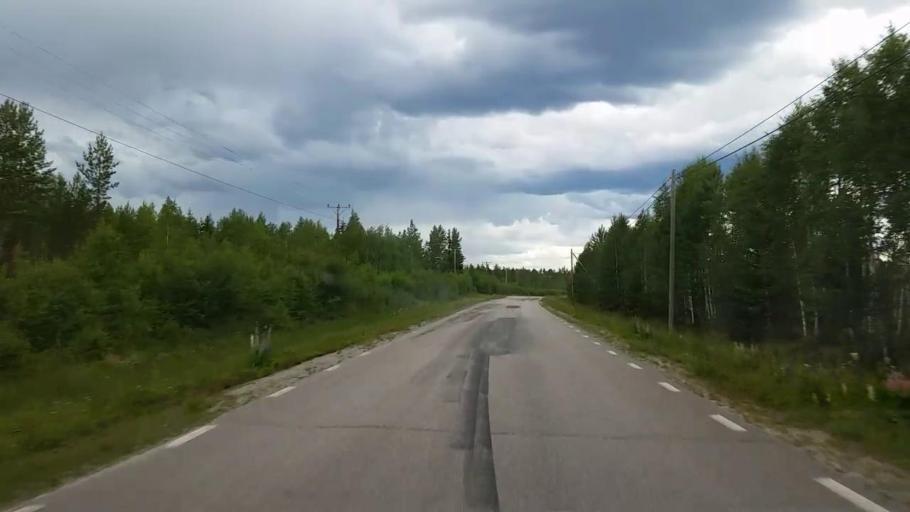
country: SE
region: Gaevleborg
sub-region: Ovanakers Kommun
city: Edsbyn
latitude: 61.4502
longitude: 15.8807
